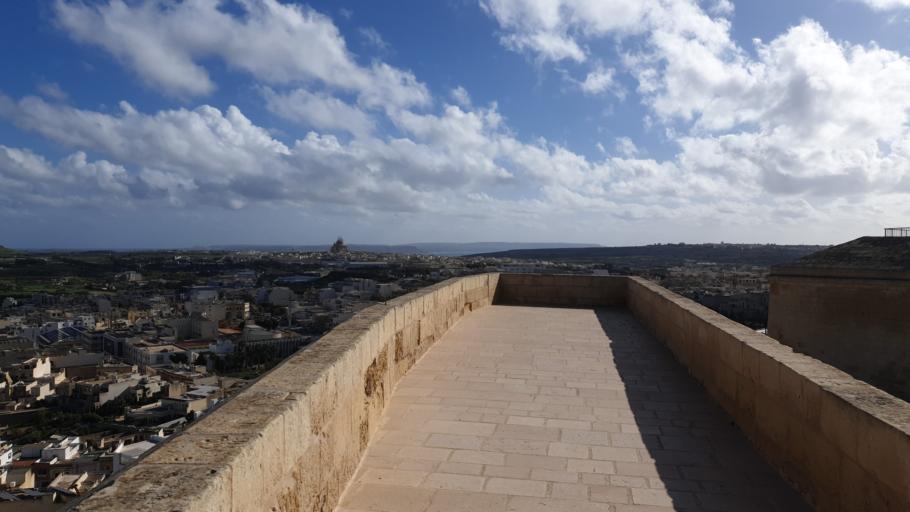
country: MT
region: Victoria
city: Victoria
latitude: 36.0469
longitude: 14.2402
